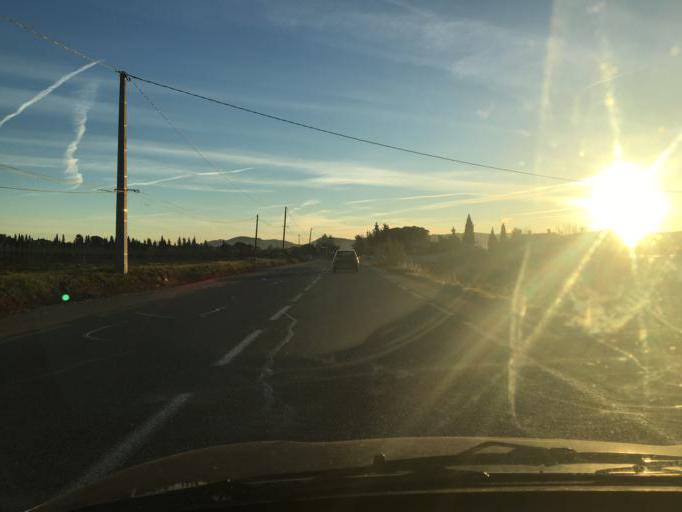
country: FR
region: Provence-Alpes-Cote d'Azur
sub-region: Departement du Var
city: Les Arcs
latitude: 43.4495
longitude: 6.4694
